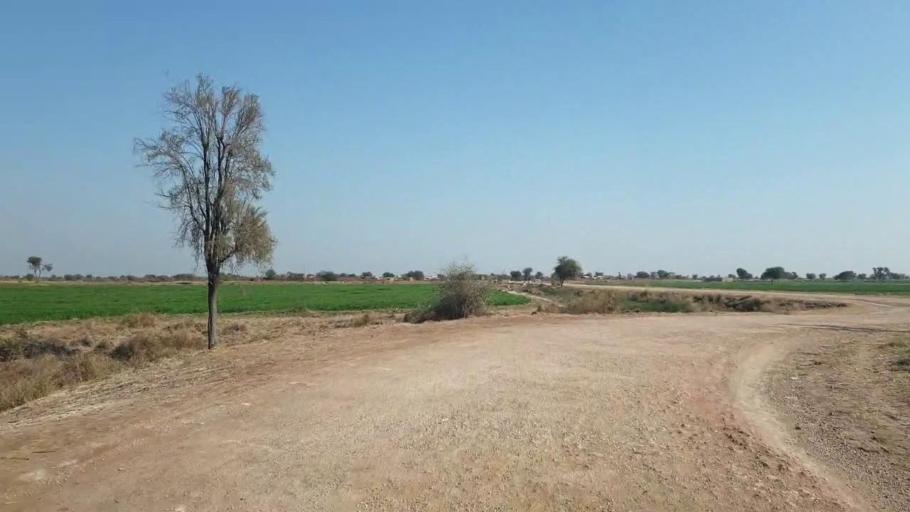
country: PK
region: Sindh
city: Shahdadpur
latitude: 25.9798
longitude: 68.6594
